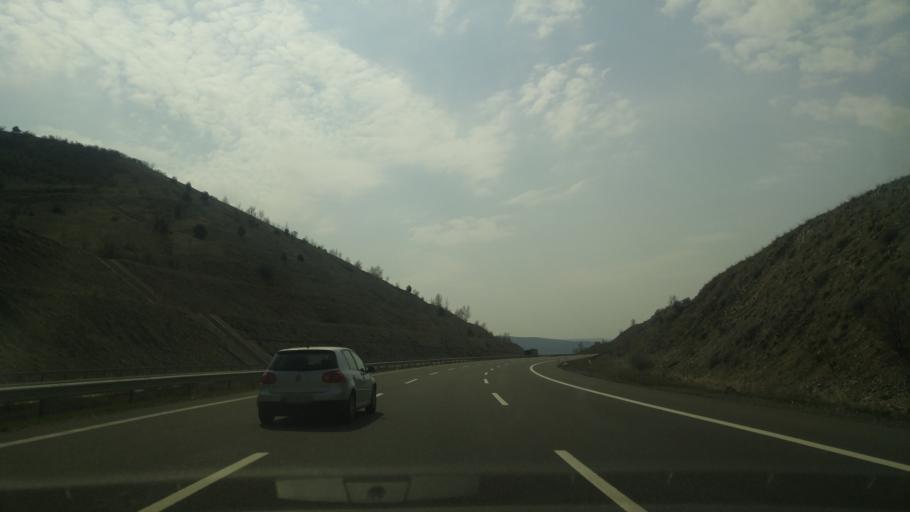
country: TR
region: Ankara
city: Celtikci
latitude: 40.3576
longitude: 32.4684
